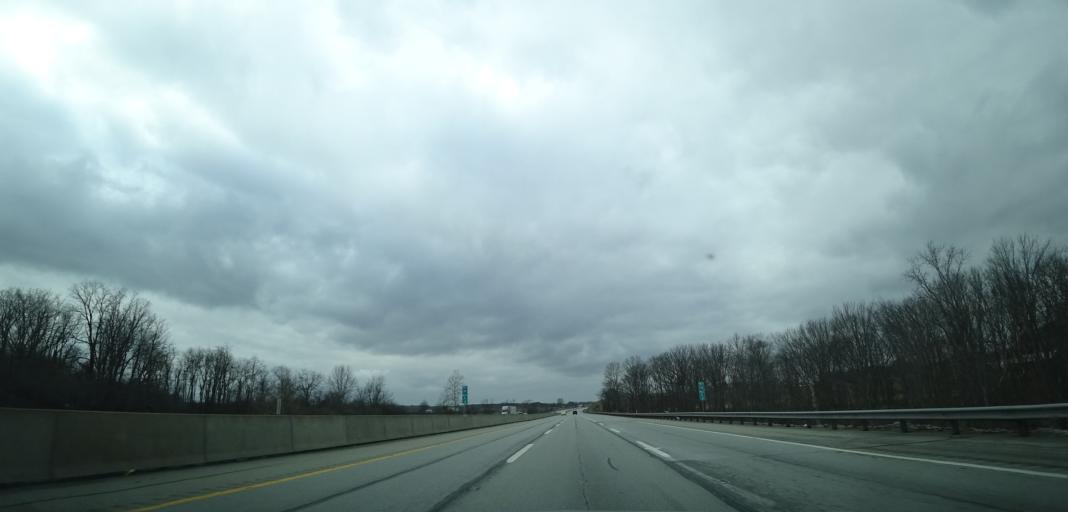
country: US
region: Pennsylvania
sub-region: Lawrence County
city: New Beaver
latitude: 40.8898
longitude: -80.4487
